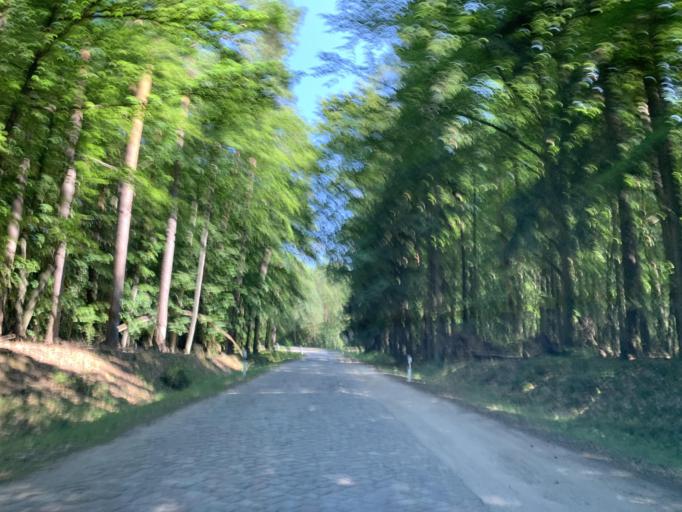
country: DE
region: Mecklenburg-Vorpommern
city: Carpin
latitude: 53.3169
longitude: 13.3215
